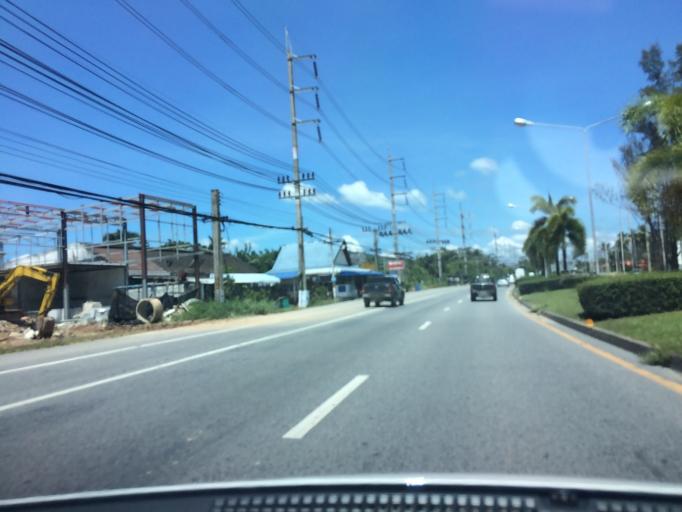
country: TH
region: Phuket
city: Thalang
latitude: 8.1044
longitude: 98.3345
